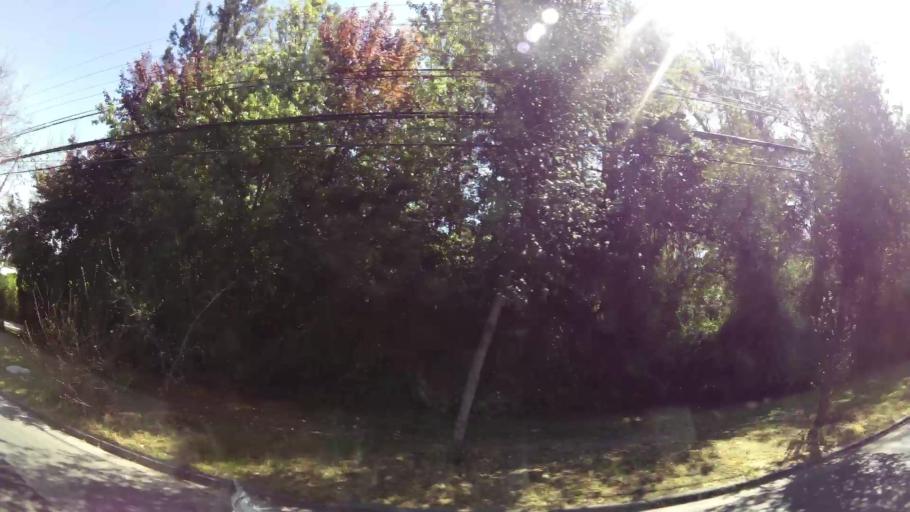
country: CL
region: Santiago Metropolitan
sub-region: Provincia de Santiago
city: Villa Presidente Frei, Nunoa, Santiago, Chile
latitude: -33.4349
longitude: -70.5221
